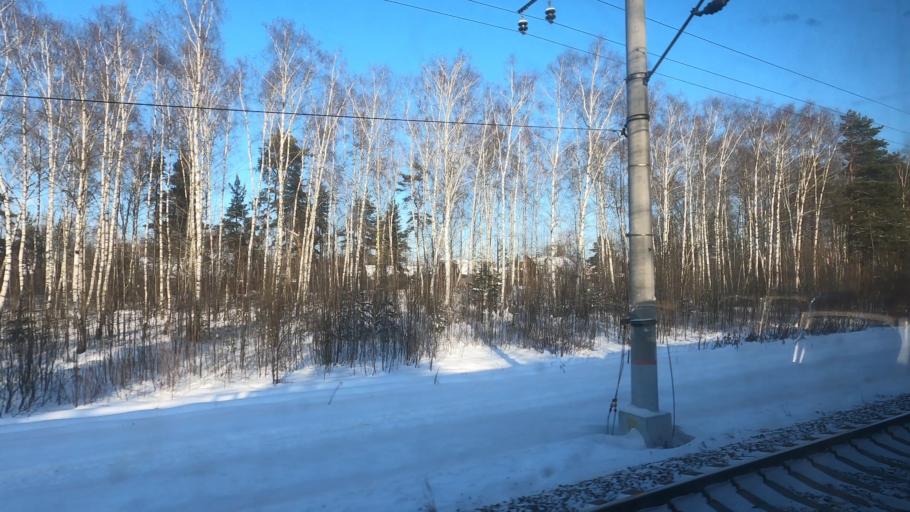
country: RU
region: Moskovskaya
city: Imeni Vorovskogo
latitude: 55.7220
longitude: 38.3025
